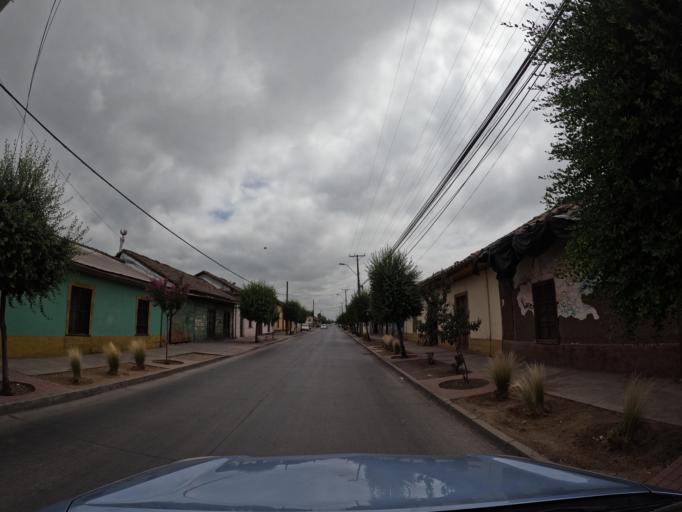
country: CL
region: O'Higgins
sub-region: Provincia de Colchagua
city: Chimbarongo
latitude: -34.7132
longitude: -71.0468
